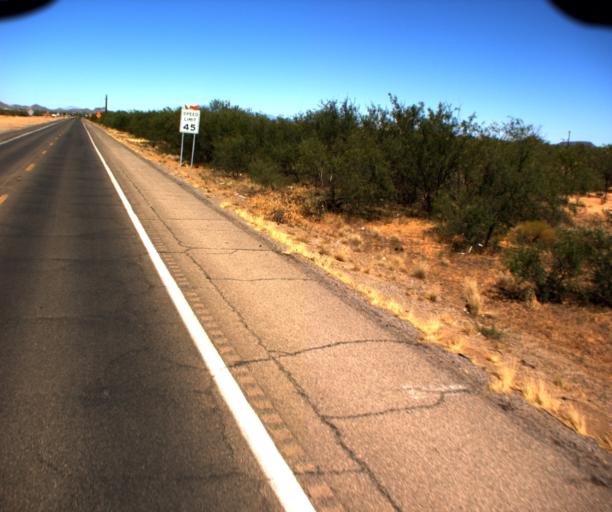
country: US
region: Arizona
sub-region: Pima County
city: Valencia West
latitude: 32.1402
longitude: -111.1519
